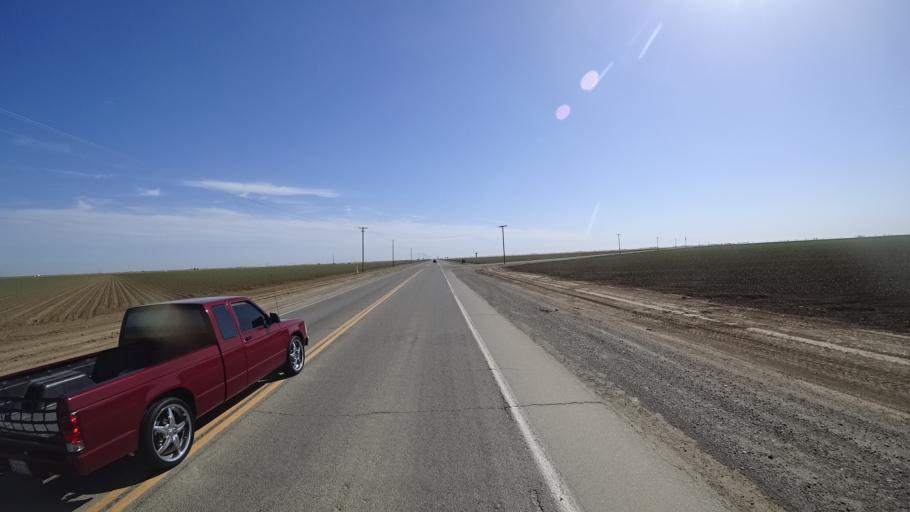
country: US
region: California
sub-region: Kings County
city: Lemoore Station
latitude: 36.1888
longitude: -119.9462
